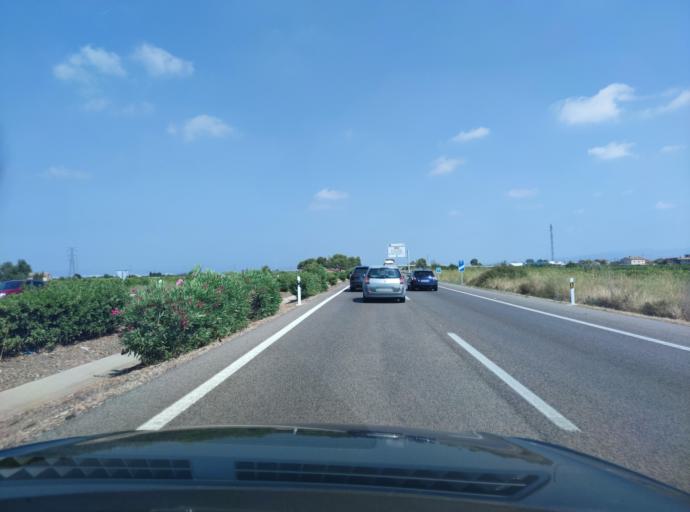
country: ES
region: Valencia
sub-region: Provincia de Castello
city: Alquerias del Nino Perdido
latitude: 39.8920
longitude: -0.1291
